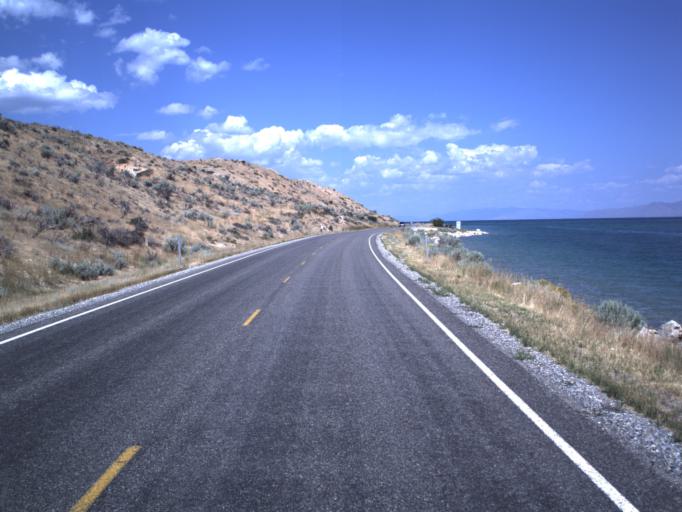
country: US
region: Utah
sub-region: Rich County
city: Randolph
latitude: 41.8707
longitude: -111.3654
